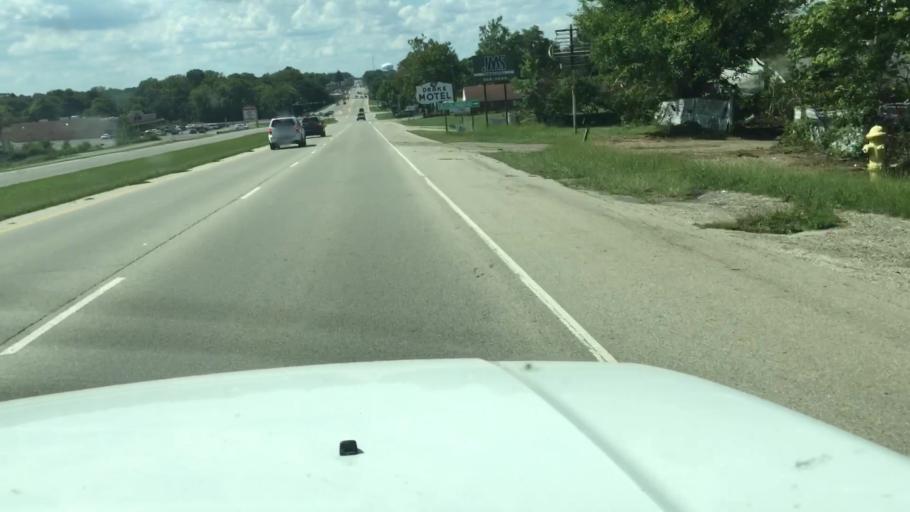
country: US
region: Ohio
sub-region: Clark County
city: Springfield
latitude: 39.9234
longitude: -83.7548
